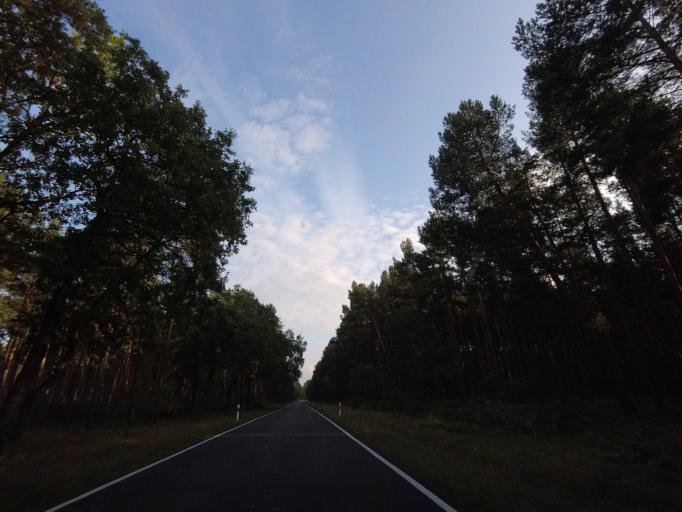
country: DE
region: Brandenburg
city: Treuenbrietzen
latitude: 52.1143
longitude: 12.8772
